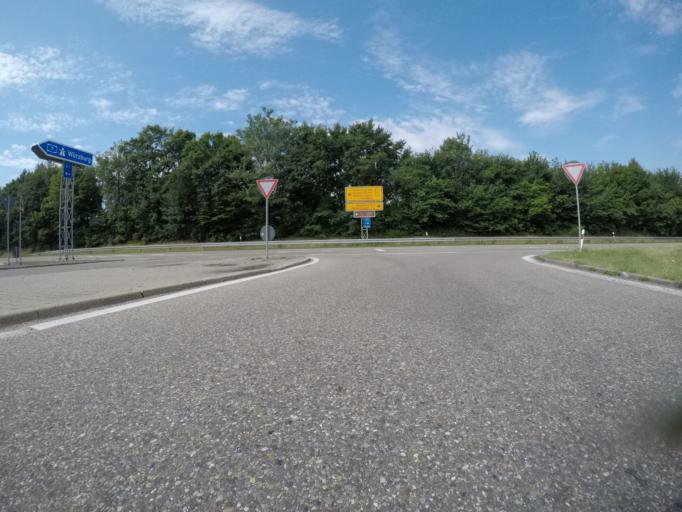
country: DE
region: Baden-Wuerttemberg
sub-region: Tuebingen Region
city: Setzingen
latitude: 48.5717
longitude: 10.1578
